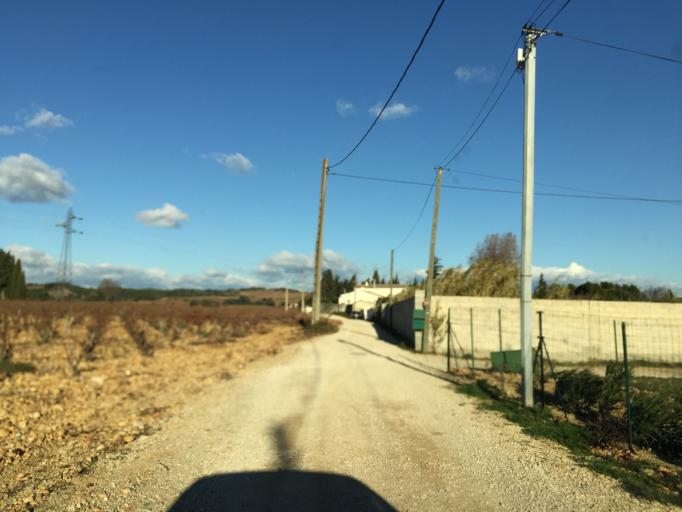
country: FR
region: Provence-Alpes-Cote d'Azur
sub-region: Departement du Vaucluse
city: Sorgues
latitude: 44.0290
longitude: 4.8582
